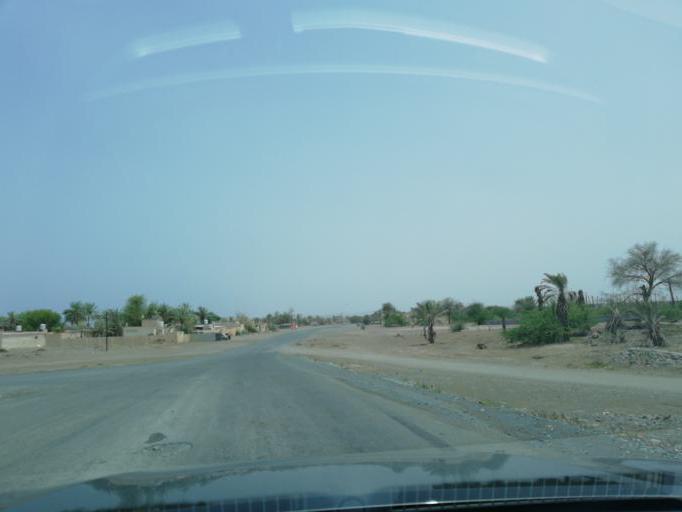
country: OM
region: Al Batinah
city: Al Liwa'
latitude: 24.6212
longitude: 56.5330
